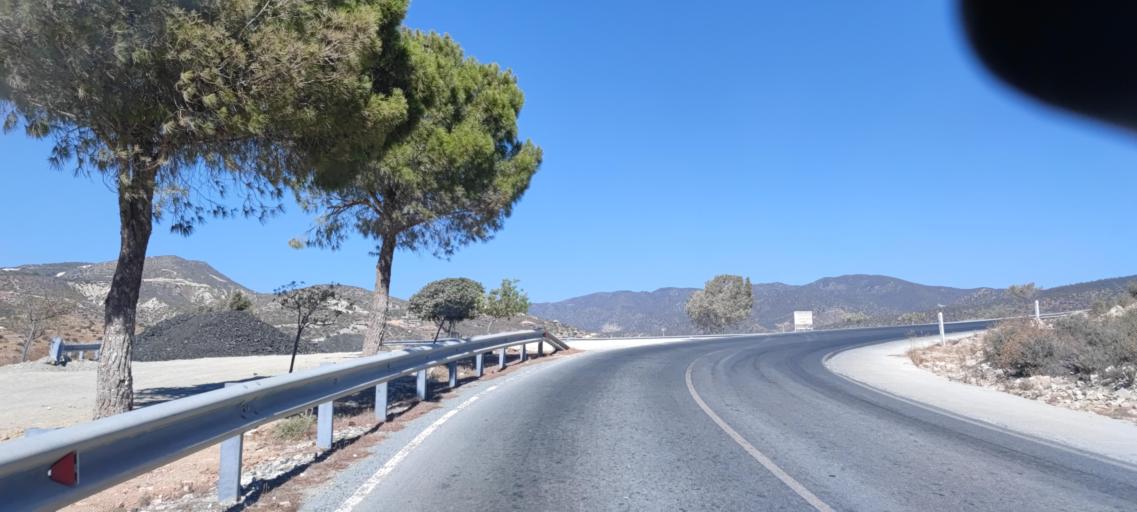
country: CY
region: Limassol
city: Mouttagiaka
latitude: 34.7434
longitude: 33.0873
